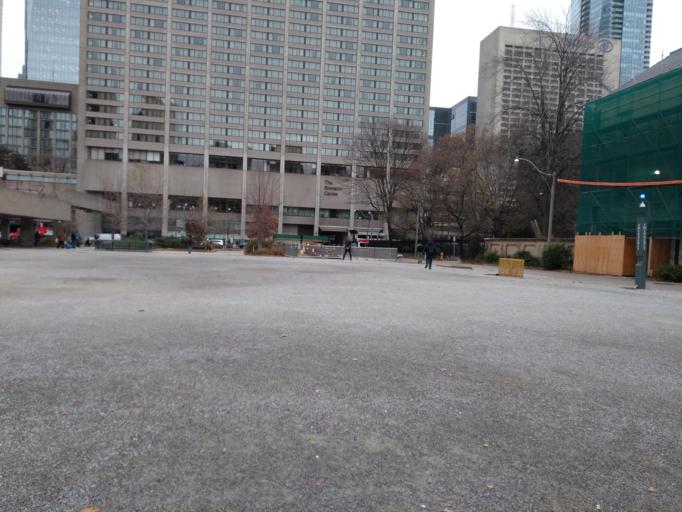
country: CA
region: Ontario
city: Toronto
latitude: 43.6523
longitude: -79.3846
